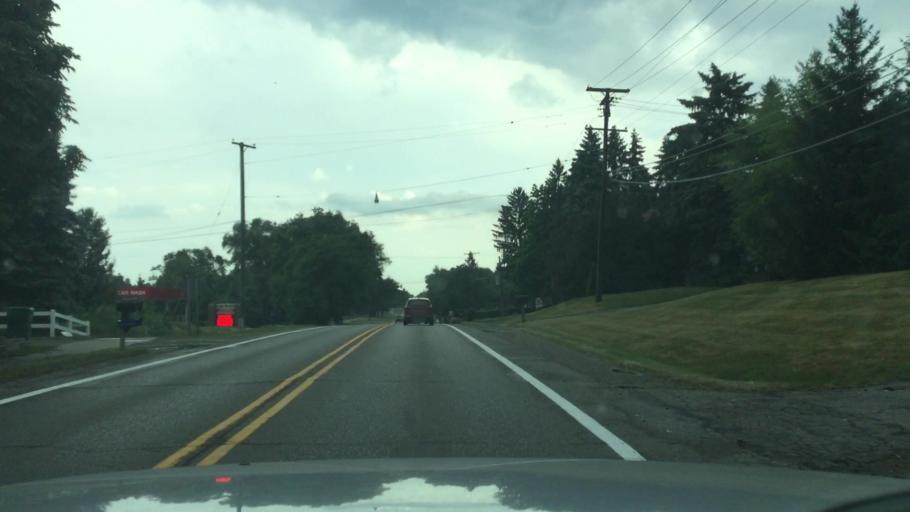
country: US
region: Michigan
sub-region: Oakland County
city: Sylvan Lake
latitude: 42.6685
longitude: -83.3472
